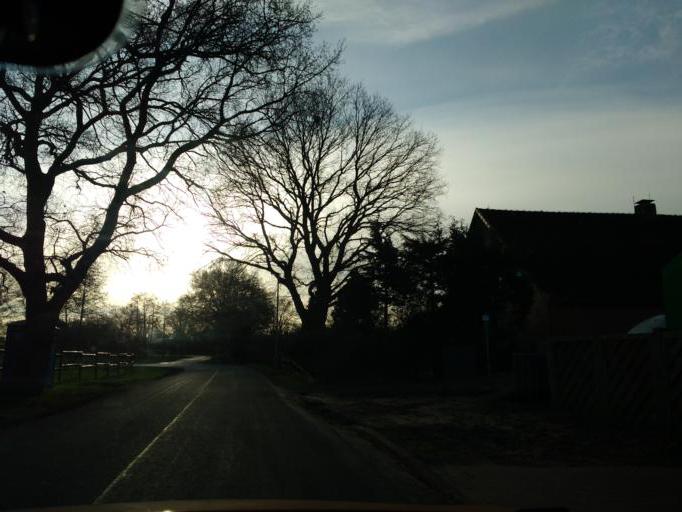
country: DE
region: Lower Saxony
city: Hatten
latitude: 53.1207
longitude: 8.3477
